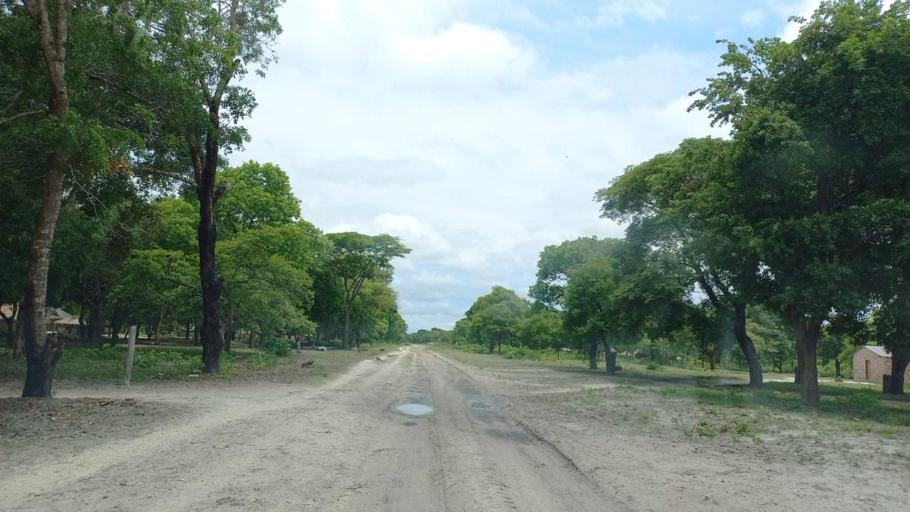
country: ZM
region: North-Western
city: Kabompo
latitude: -13.1871
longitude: 23.9564
